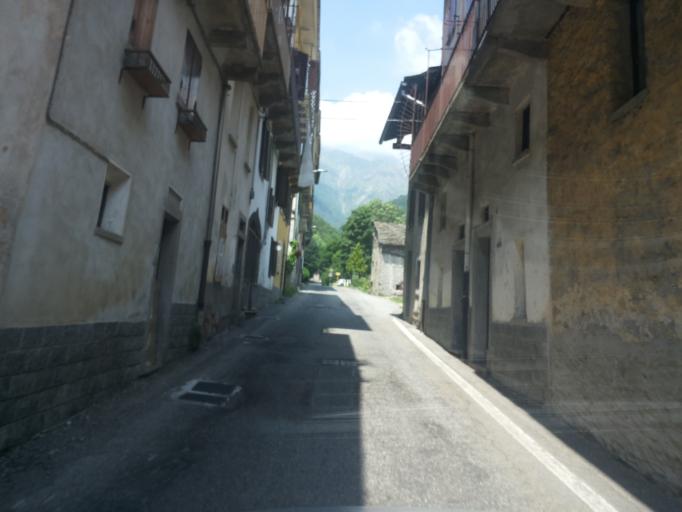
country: IT
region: Piedmont
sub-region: Provincia di Biella
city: Rosazza
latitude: 45.6788
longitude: 7.9754
